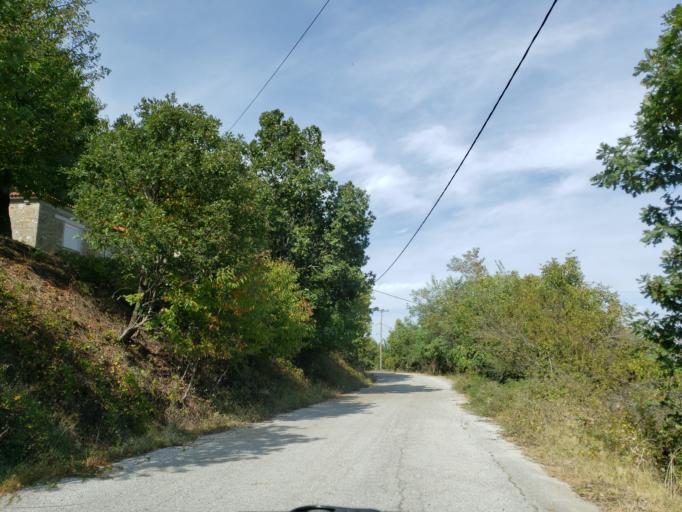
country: GR
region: Thessaly
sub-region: Trikala
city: Kastraki
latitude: 39.7730
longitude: 21.6612
